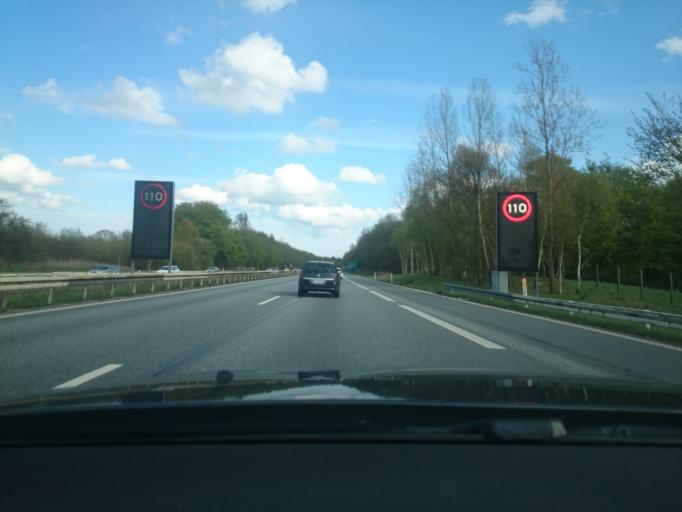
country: DK
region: Capital Region
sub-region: Fureso Kommune
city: Vaerlose
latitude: 55.7758
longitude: 12.4067
